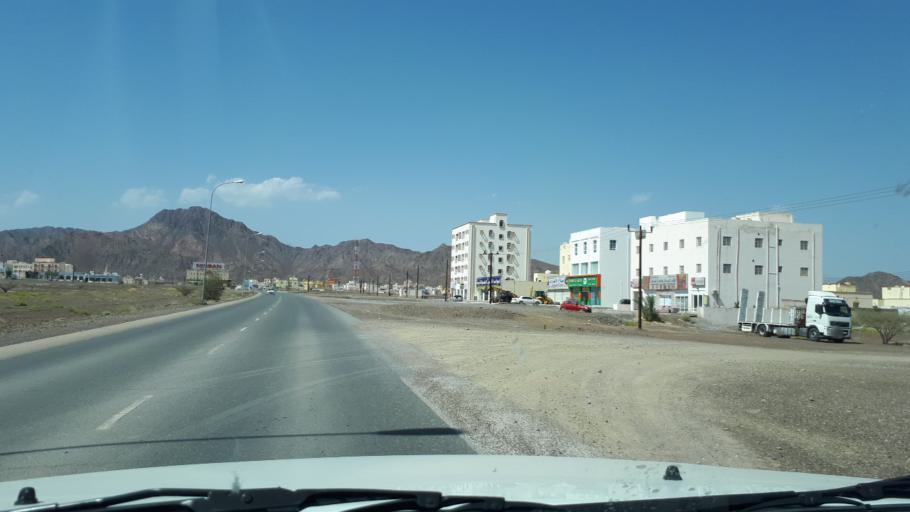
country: OM
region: Muhafazat ad Dakhiliyah
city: Bahla'
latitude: 22.9431
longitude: 57.2596
